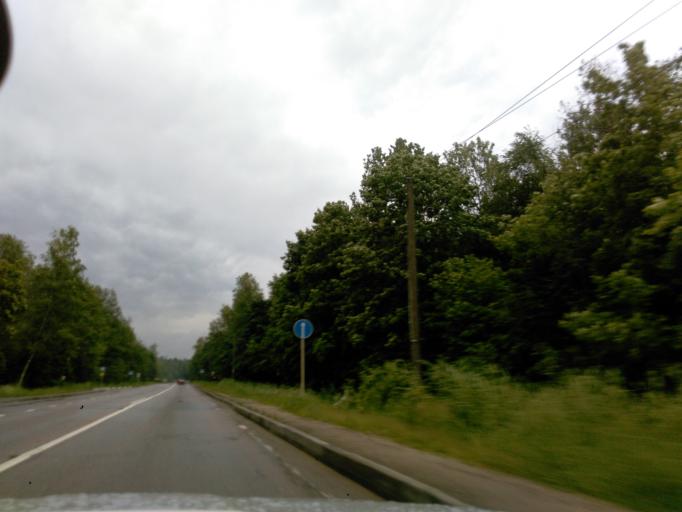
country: RU
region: Moskovskaya
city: Povarovo
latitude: 56.0051
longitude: 37.0273
